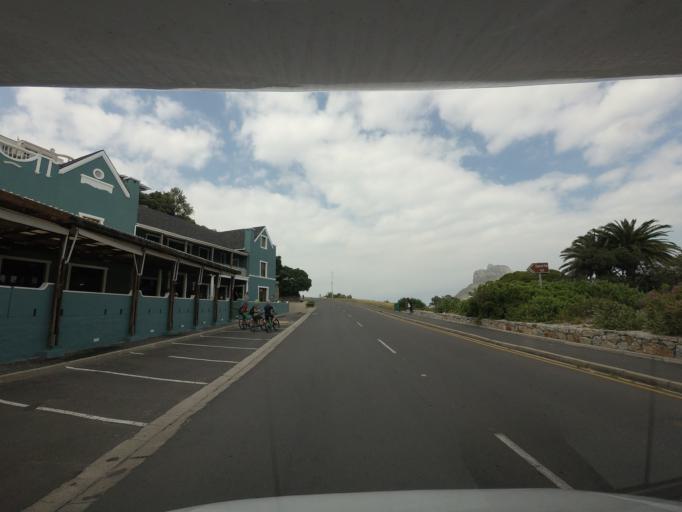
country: ZA
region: Western Cape
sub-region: City of Cape Town
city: Constantia
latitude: -34.0468
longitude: 18.3617
